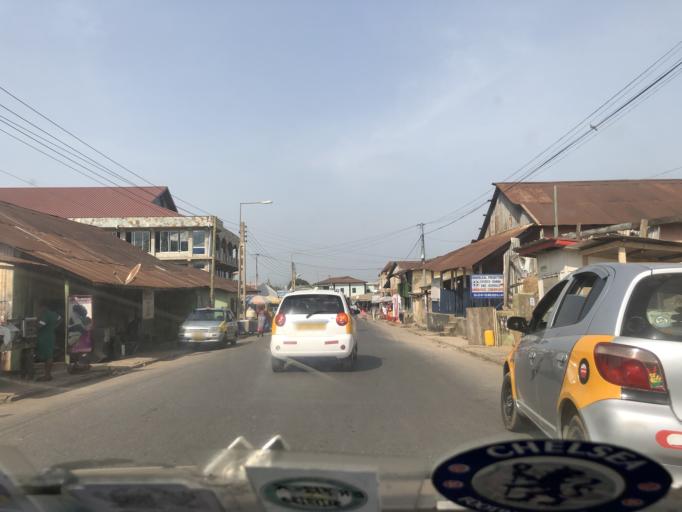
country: GH
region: Eastern
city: Koforidua
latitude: 6.0958
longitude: -0.2585
